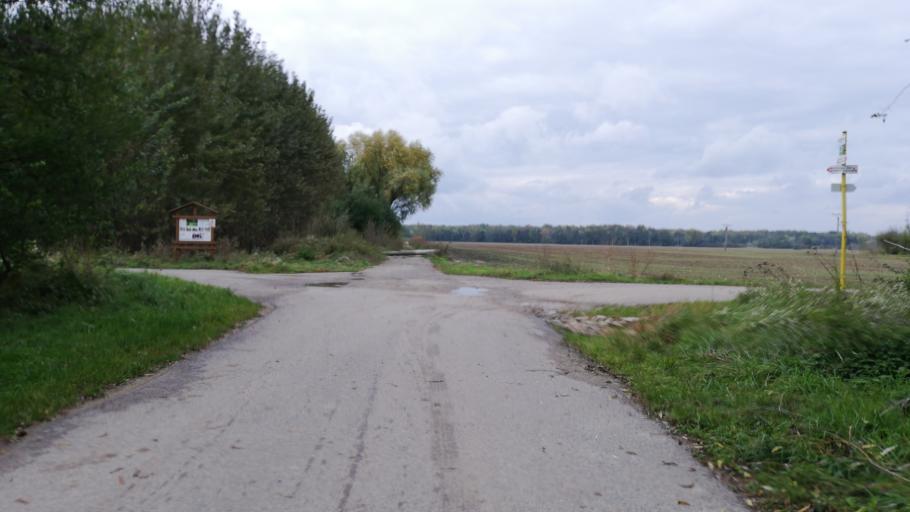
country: SK
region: Trnavsky
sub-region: Okres Skalica
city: Skalica
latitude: 48.8420
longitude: 17.1920
